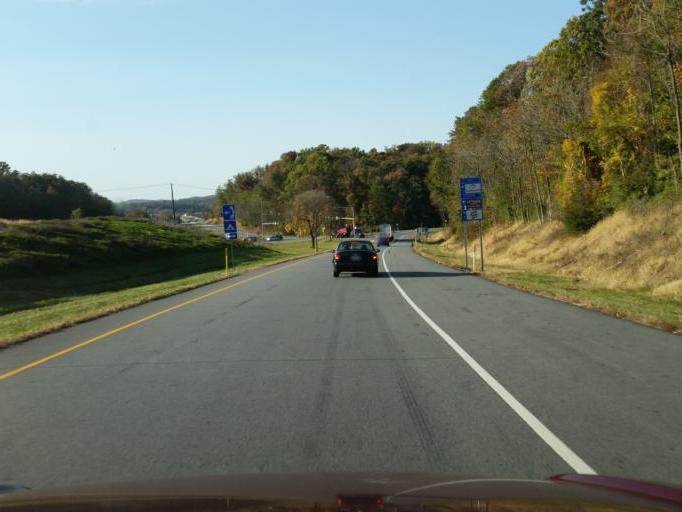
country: US
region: Pennsylvania
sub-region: Lancaster County
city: Elizabethtown
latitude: 40.1772
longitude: -76.5990
